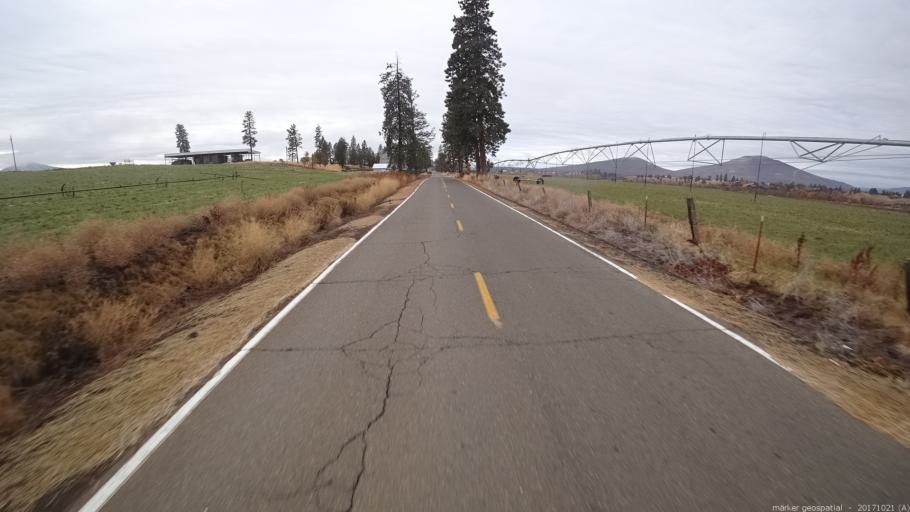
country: US
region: California
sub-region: Shasta County
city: Burney
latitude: 41.0203
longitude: -121.4104
